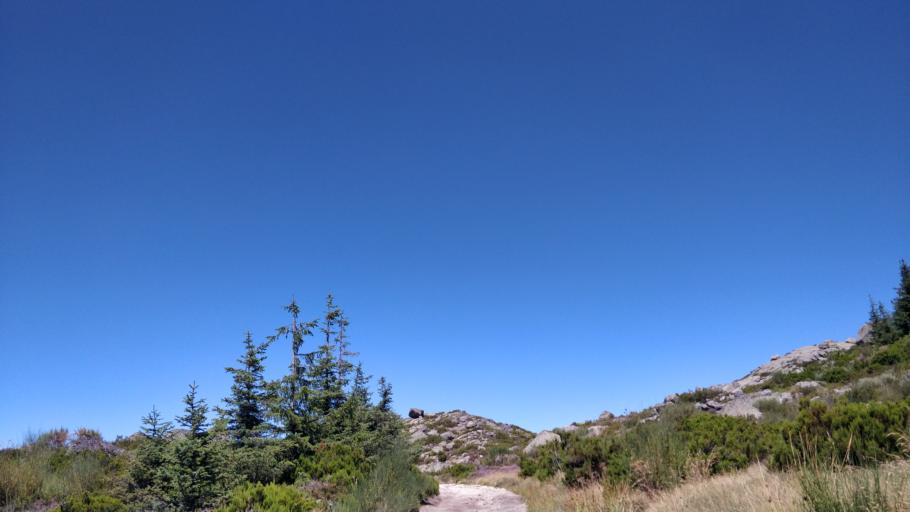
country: PT
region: Guarda
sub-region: Seia
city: Seia
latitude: 40.3635
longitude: -7.6300
